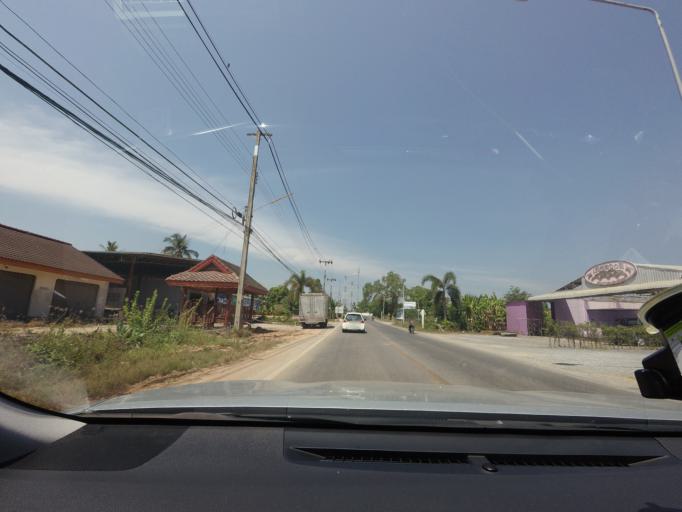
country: TH
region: Surat Thani
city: Phunphin
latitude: 9.1916
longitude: 99.2547
